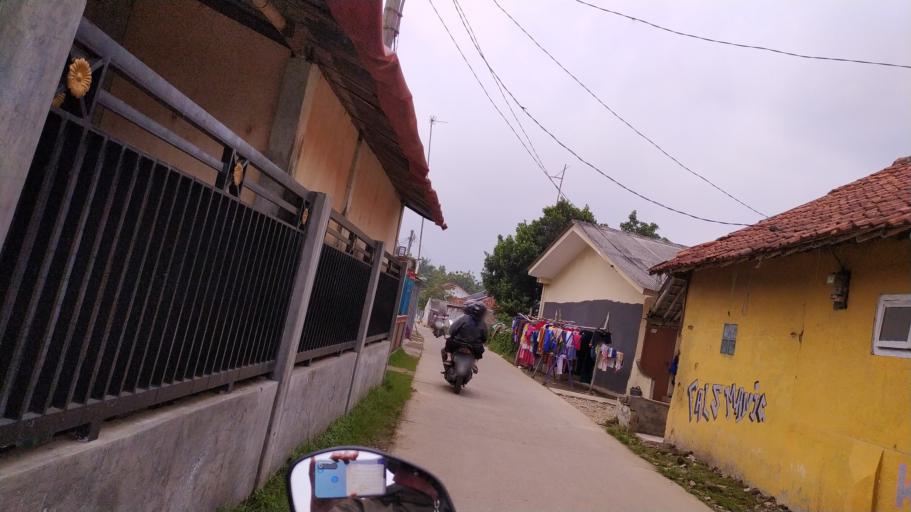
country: ID
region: West Java
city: Ciampea
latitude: -6.5803
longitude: 106.7237
